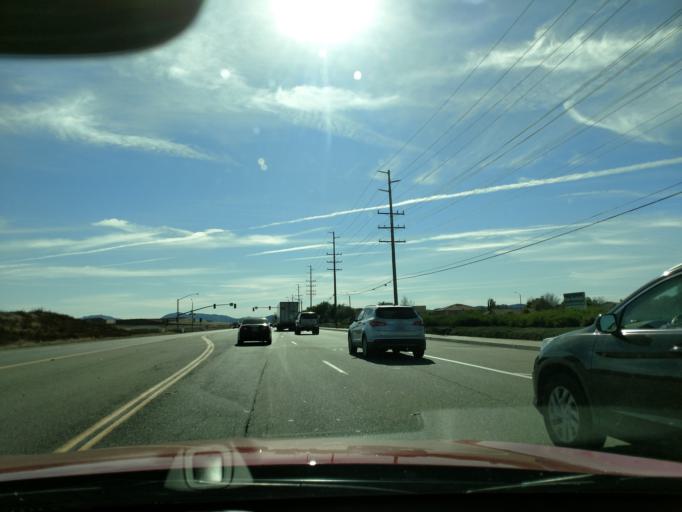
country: US
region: California
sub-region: Riverside County
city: Murrieta Hot Springs
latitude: 33.5775
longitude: -117.1343
